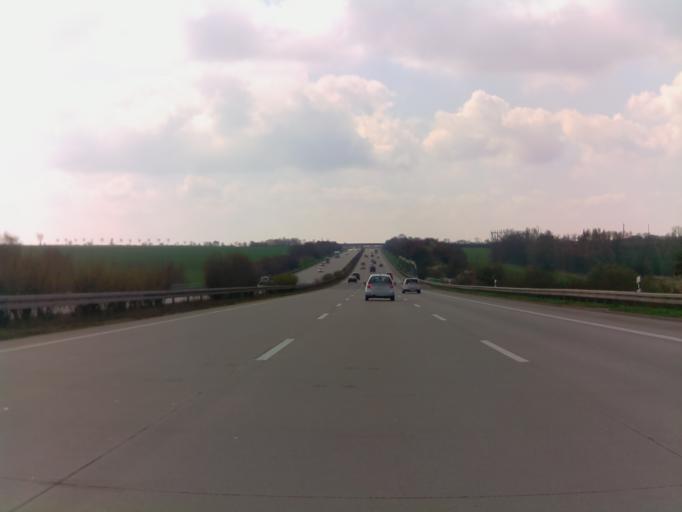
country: DE
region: Thuringia
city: Walpernhain
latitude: 51.0074
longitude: 11.9230
